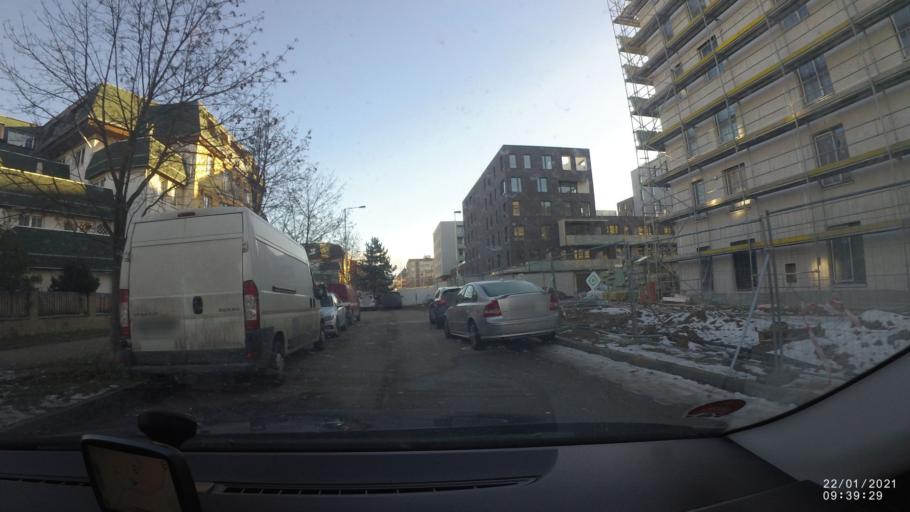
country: CZ
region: Praha
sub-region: Praha 12
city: Modrany
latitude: 50.0283
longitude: 14.3648
